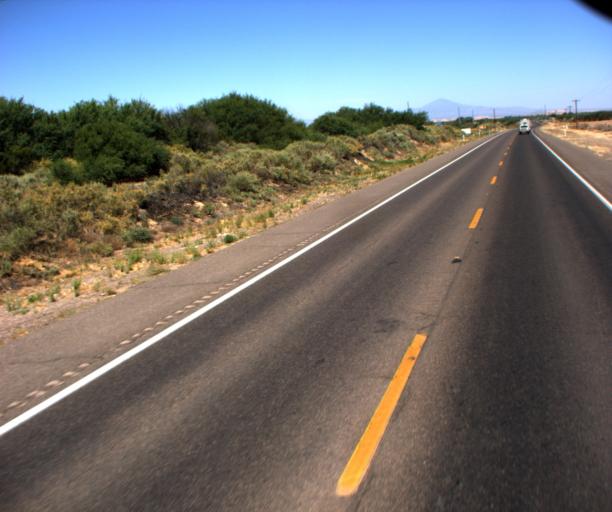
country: US
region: Arizona
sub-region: Graham County
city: Pima
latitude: 32.9283
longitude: -109.8842
